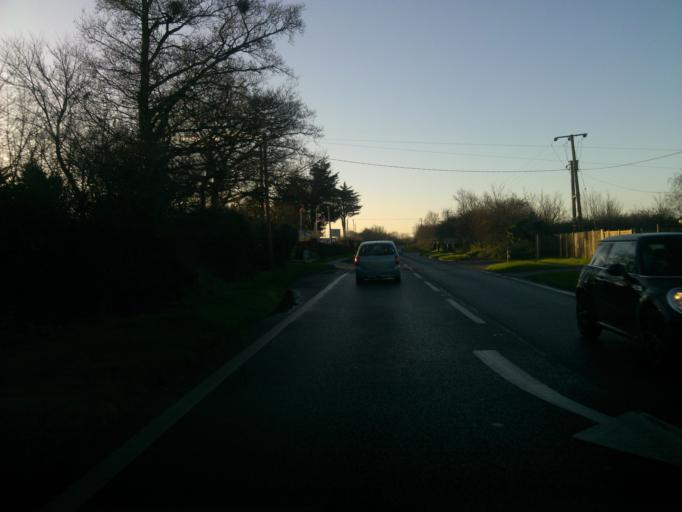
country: GB
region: England
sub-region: Essex
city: Saint Osyth
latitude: 51.8148
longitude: 1.0749
